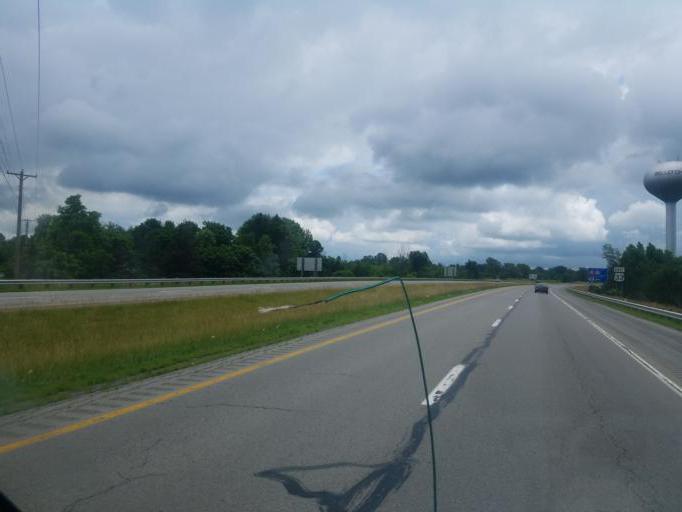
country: US
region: Ohio
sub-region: Logan County
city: Bellefontaine
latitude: 40.3781
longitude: -83.7476
